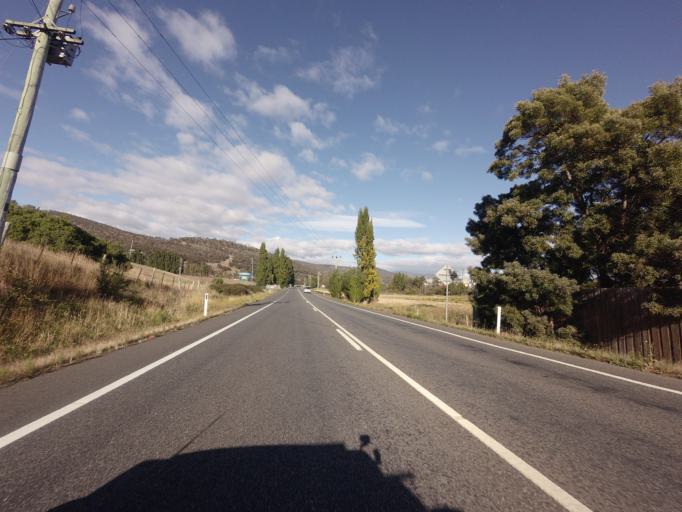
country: AU
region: Tasmania
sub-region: Derwent Valley
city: New Norfolk
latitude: -42.7779
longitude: 147.1137
